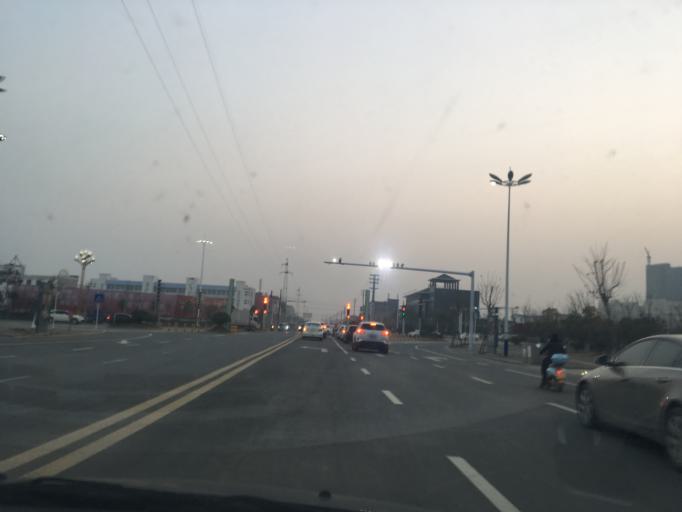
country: CN
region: Hubei
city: Macheng
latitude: 31.1622
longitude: 115.0188
